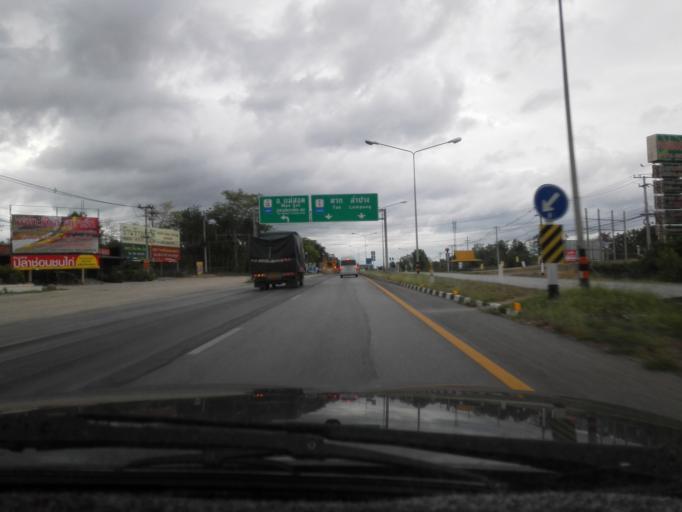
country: TH
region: Tak
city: Tak
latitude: 16.8394
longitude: 99.1148
